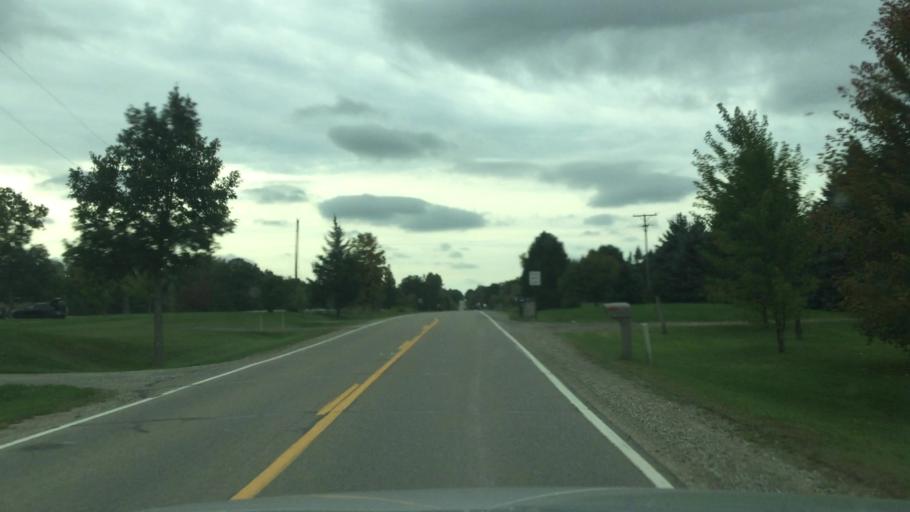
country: US
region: Michigan
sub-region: Livingston County
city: Howell
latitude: 42.6715
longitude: -83.8771
